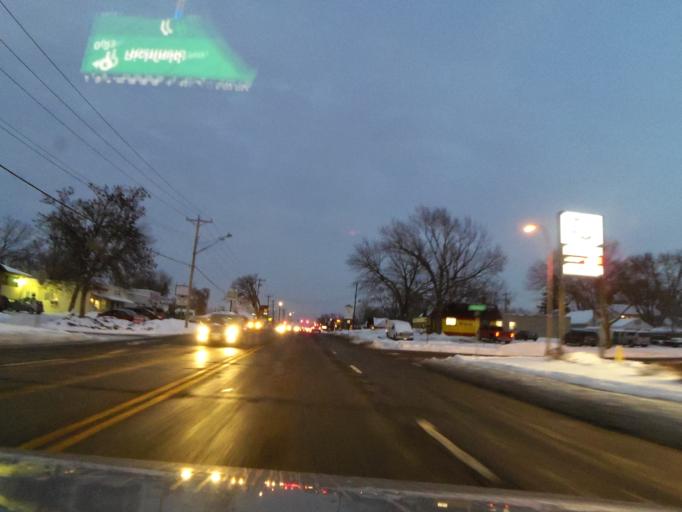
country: US
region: Minnesota
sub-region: Hennepin County
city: Richfield
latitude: 44.8835
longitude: -93.2573
